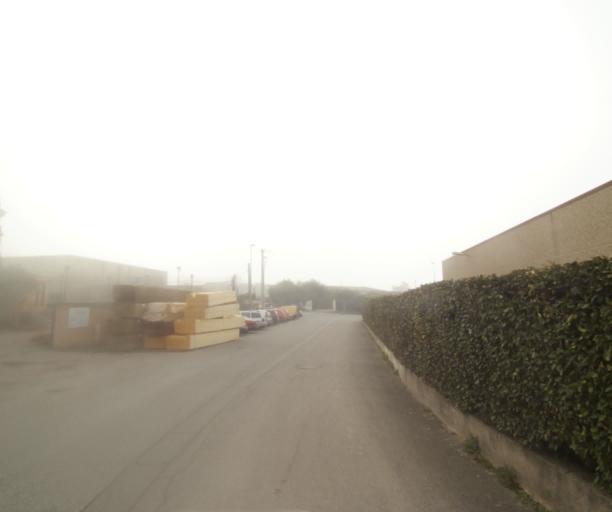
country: FR
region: Provence-Alpes-Cote d'Azur
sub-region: Departement des Bouches-du-Rhone
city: Eguilles
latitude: 43.5466
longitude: 5.3646
